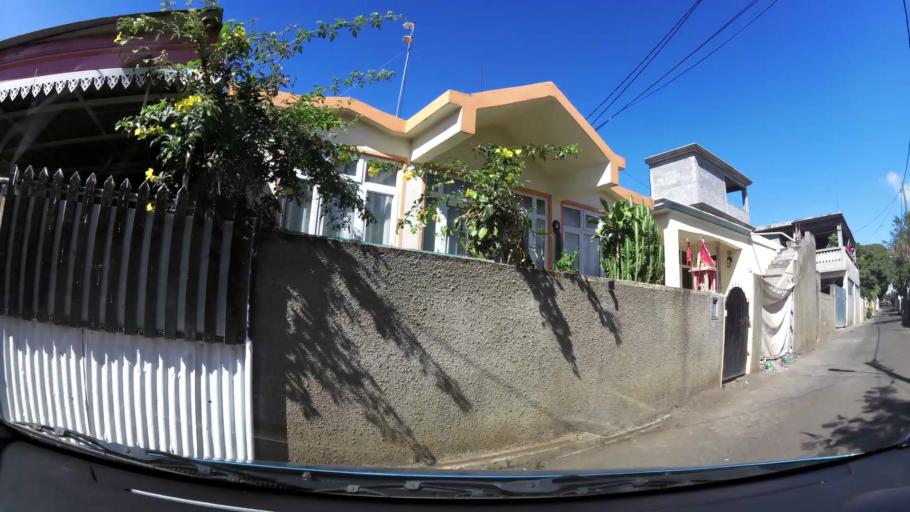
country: MU
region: Black River
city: Cascavelle
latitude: -20.2574
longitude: 57.4114
